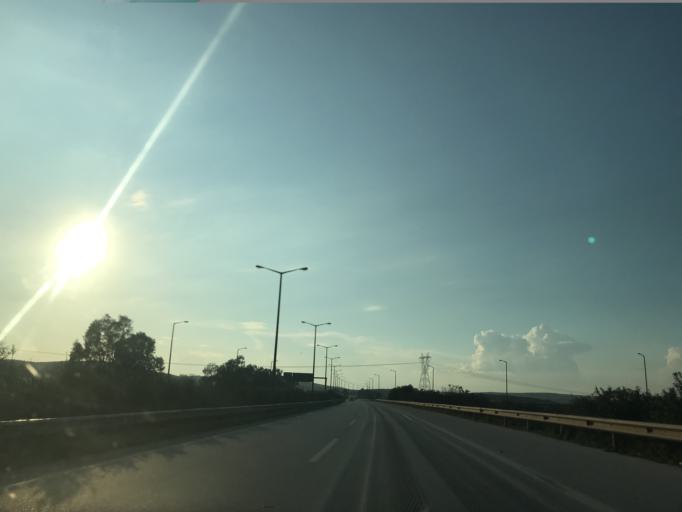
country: TR
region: Osmaniye
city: Toprakkale
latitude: 36.9753
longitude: 36.0171
